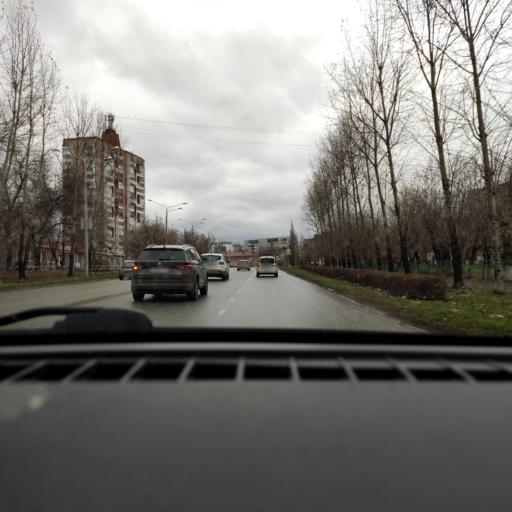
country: RU
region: Perm
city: Perm
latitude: 57.9795
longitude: 56.2157
